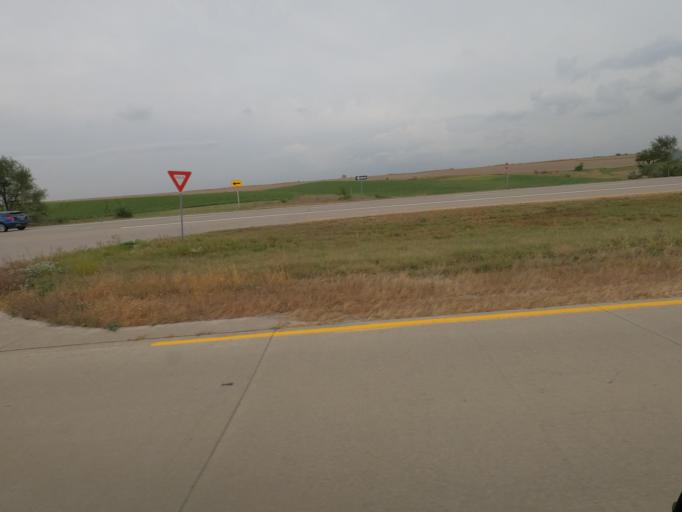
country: US
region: Iowa
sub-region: Mahaska County
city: Oskaloosa
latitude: 41.3360
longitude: -92.7297
